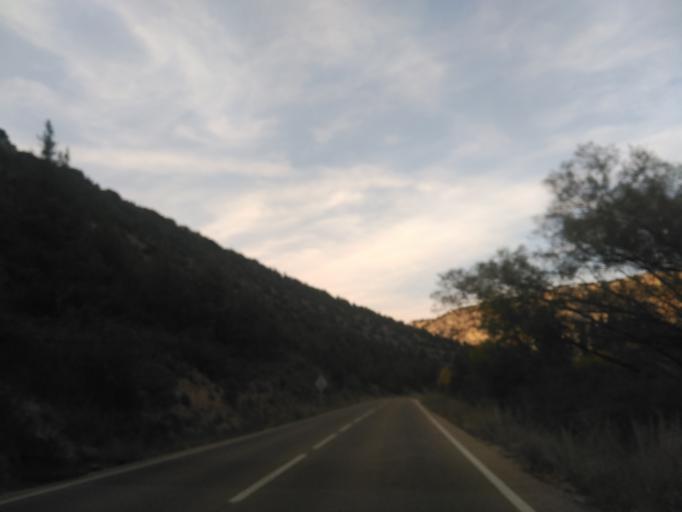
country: ES
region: Castille and Leon
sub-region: Provincia de Soria
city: Ucero
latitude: 41.7268
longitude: -3.0487
